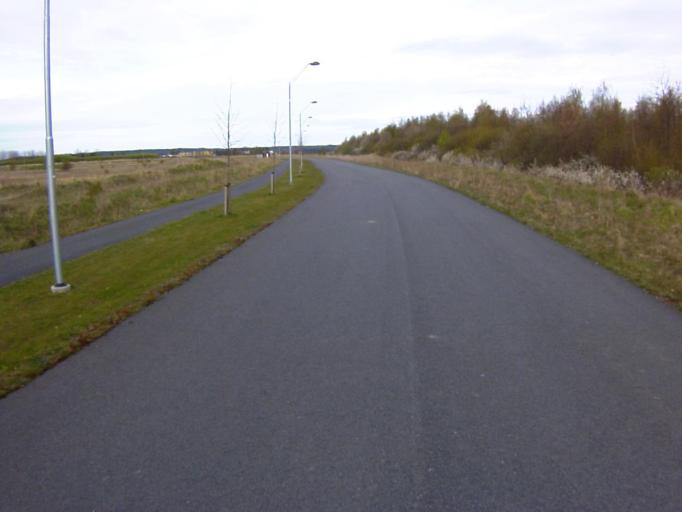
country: SE
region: Skane
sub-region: Kristianstads Kommun
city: Kristianstad
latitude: 56.0258
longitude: 14.1202
